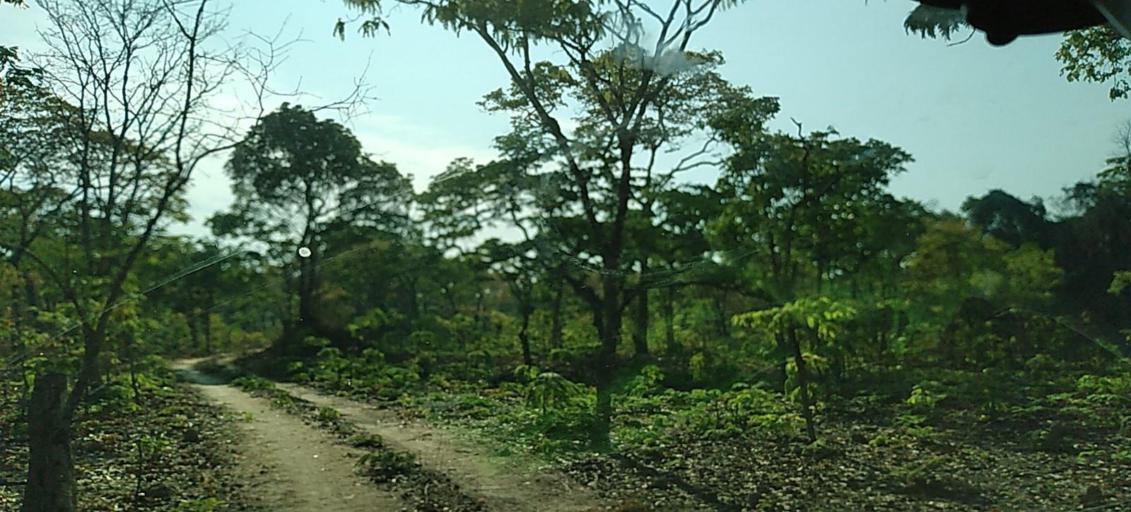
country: ZM
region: North-Western
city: Kalengwa
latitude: -13.2354
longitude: 25.0602
